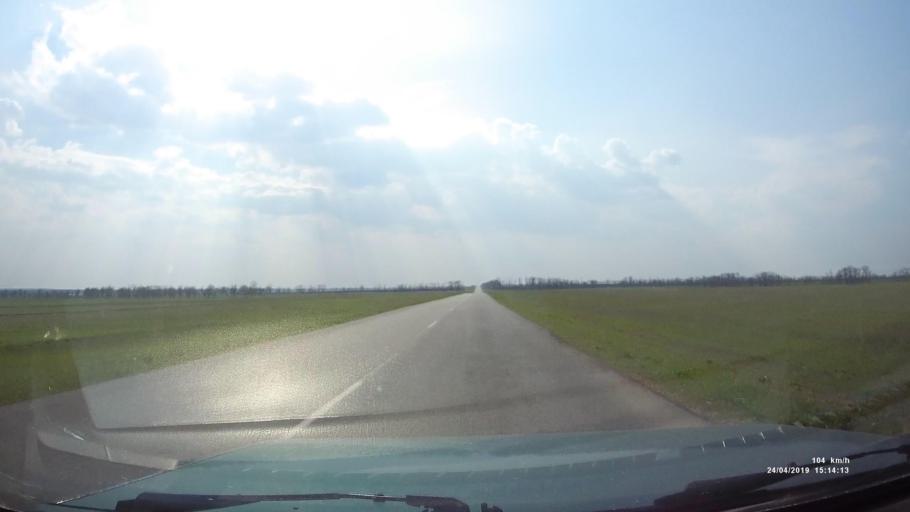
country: RU
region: Rostov
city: Remontnoye
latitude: 46.5461
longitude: 43.2627
